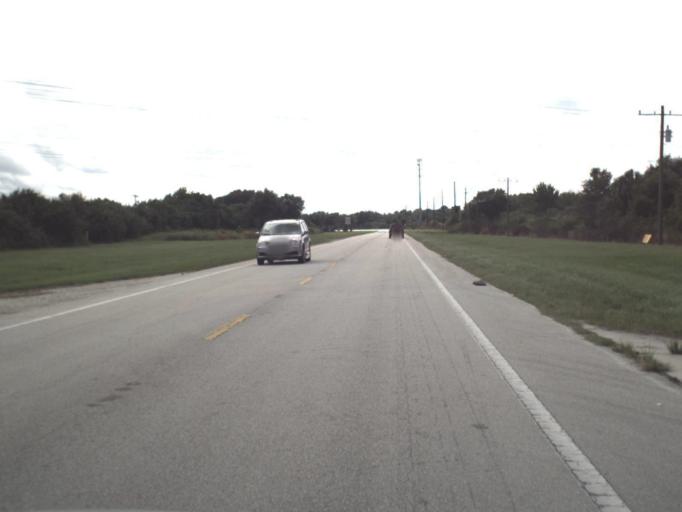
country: US
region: Florida
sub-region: Hillsborough County
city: Ruskin
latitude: 27.6034
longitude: -82.4216
